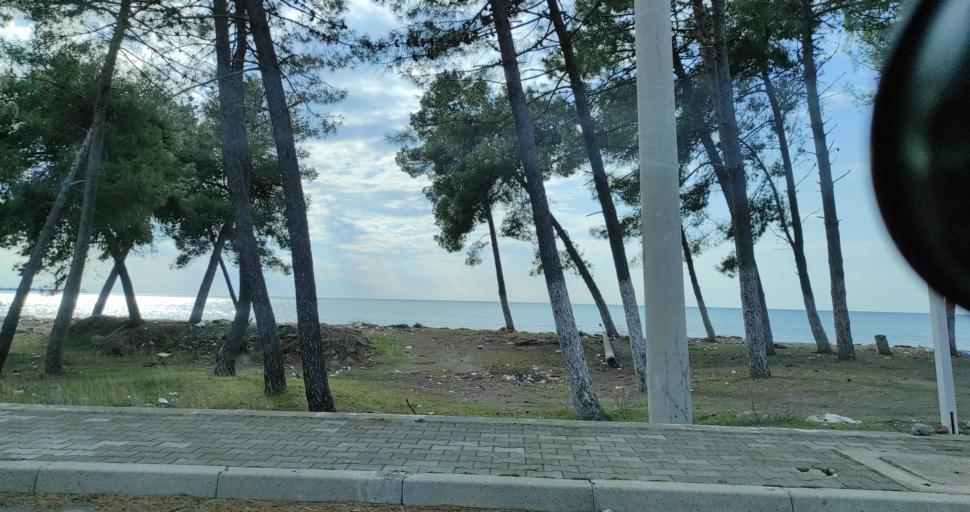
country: AL
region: Lezhe
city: Shengjin
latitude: 41.7873
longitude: 19.6033
